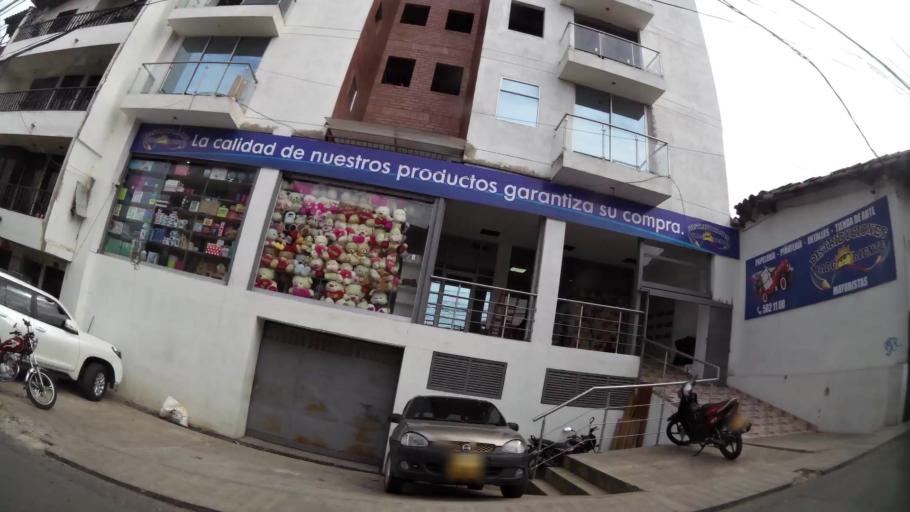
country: CO
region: Antioquia
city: Rionegro
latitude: 6.1516
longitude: -75.3757
